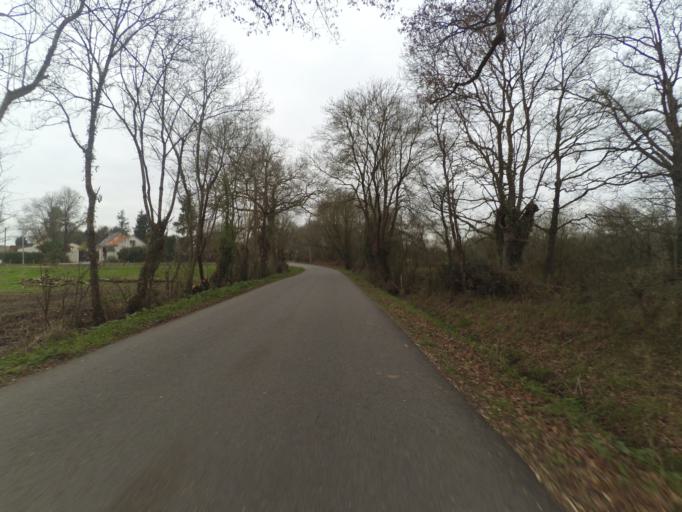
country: FR
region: Pays de la Loire
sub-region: Departement de la Loire-Atlantique
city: Coueron
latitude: 47.2402
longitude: -1.7101
